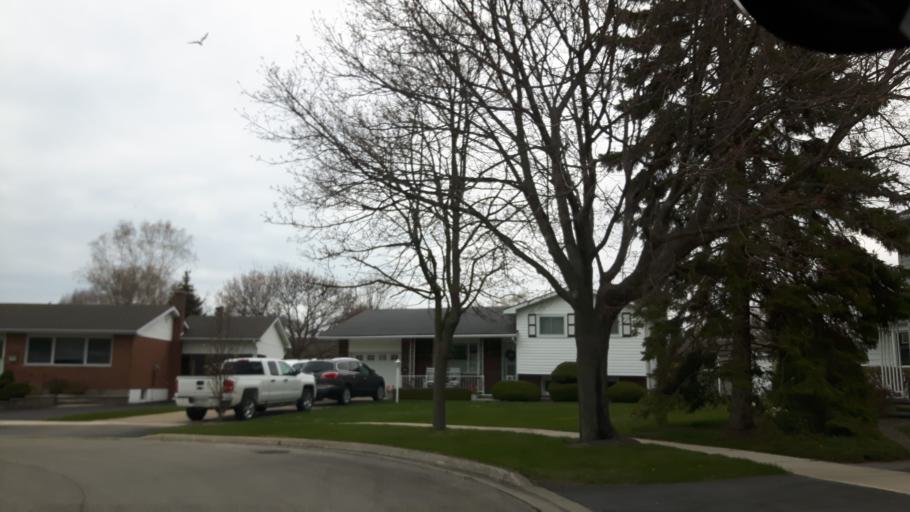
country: CA
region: Ontario
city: Goderich
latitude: 43.7344
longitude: -81.7195
